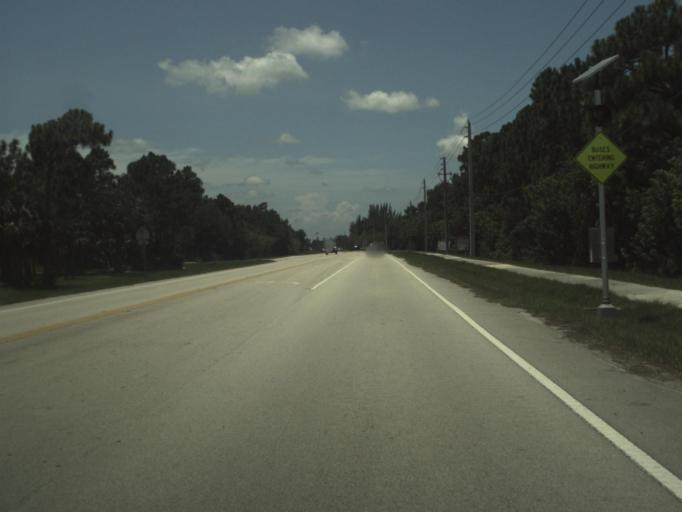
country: US
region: Florida
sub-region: Martin County
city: Port Salerno
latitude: 27.1206
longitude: -80.2411
